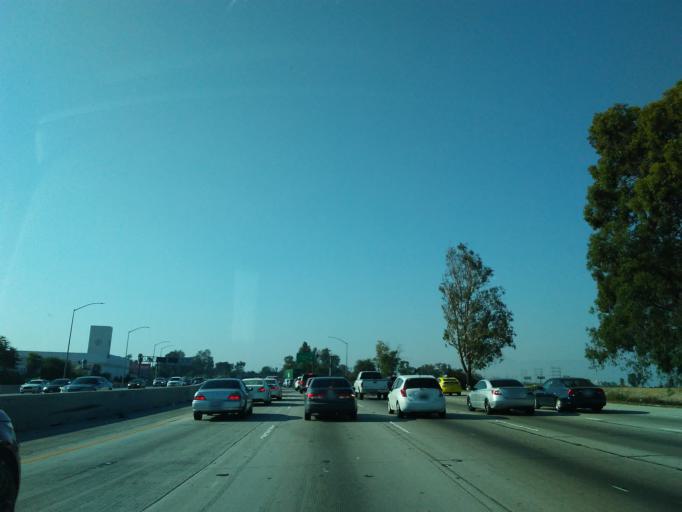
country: US
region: California
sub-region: Los Angeles County
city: East Rancho Dominguez
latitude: 33.9253
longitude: -118.1777
